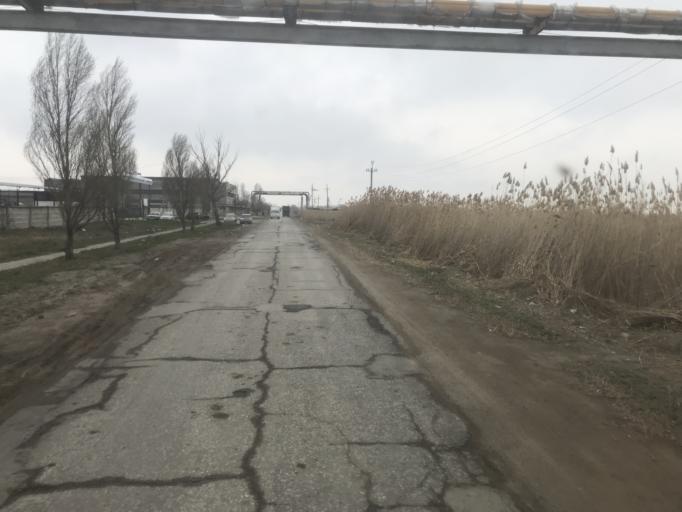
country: RU
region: Volgograd
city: Svetlyy Yar
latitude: 48.5246
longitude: 44.6170
